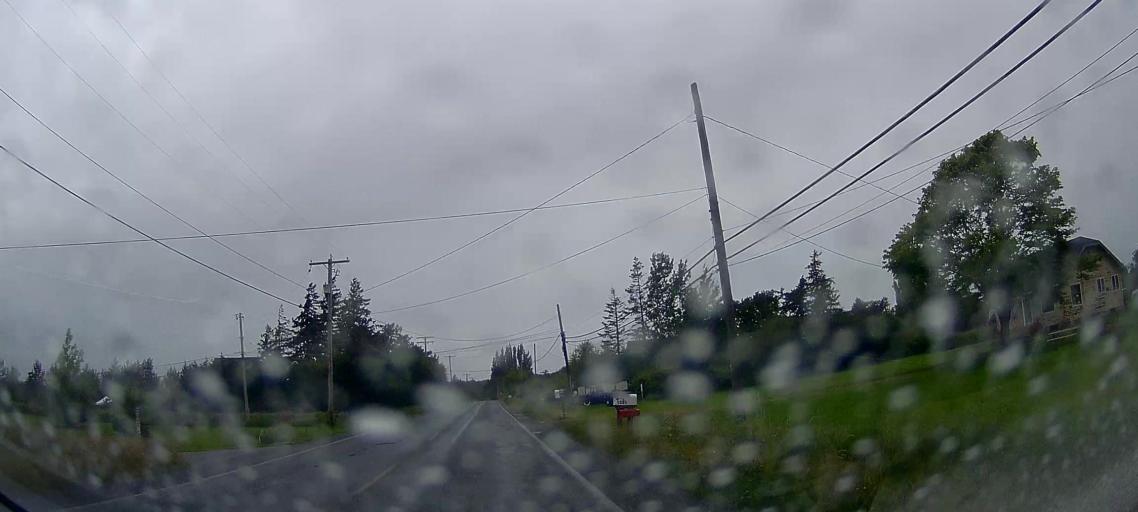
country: US
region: Washington
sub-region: Whatcom County
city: Marietta-Alderwood
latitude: 48.7832
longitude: -122.5642
